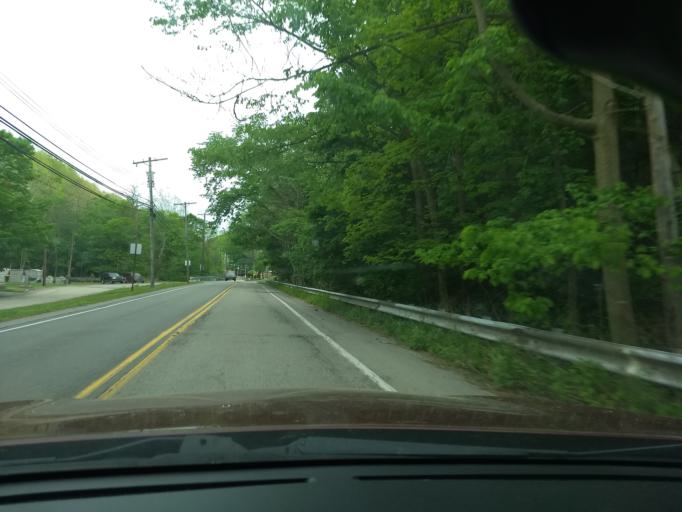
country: US
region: Pennsylvania
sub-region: Allegheny County
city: Carnegie
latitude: 40.4172
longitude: -80.1002
